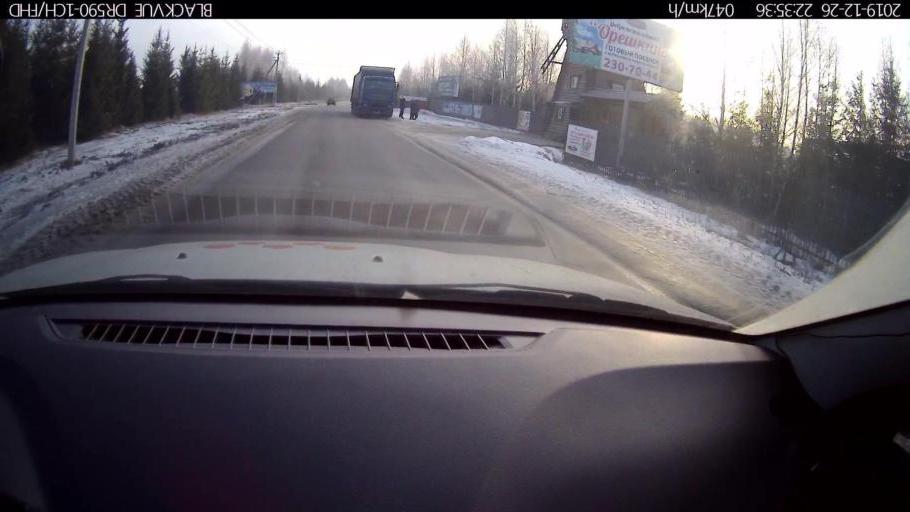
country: RU
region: Nizjnij Novgorod
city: Burevestnik
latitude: 56.1465
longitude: 43.7209
